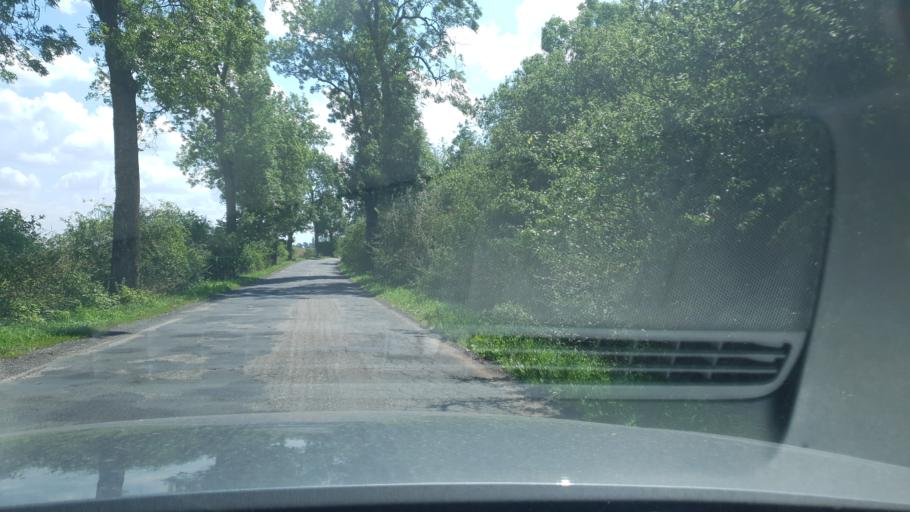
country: PL
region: Kujawsko-Pomorskie
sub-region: Powiat wabrzeski
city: Pluznica
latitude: 53.3560
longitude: 18.8206
